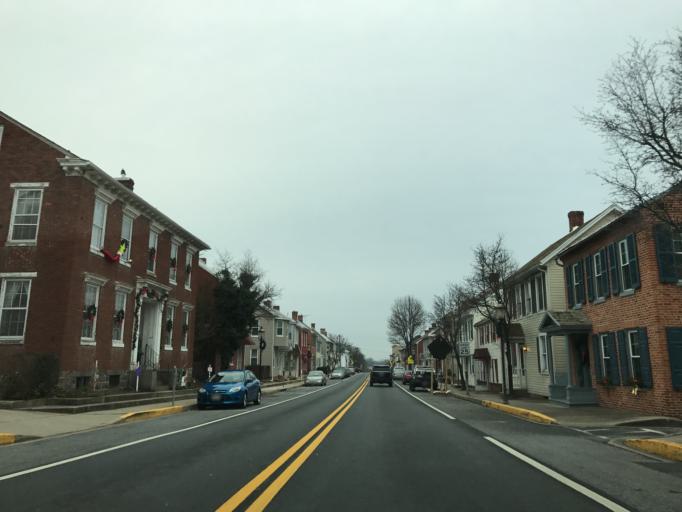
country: US
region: Maryland
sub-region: Frederick County
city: Emmitsburg
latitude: 39.7044
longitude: -77.3257
